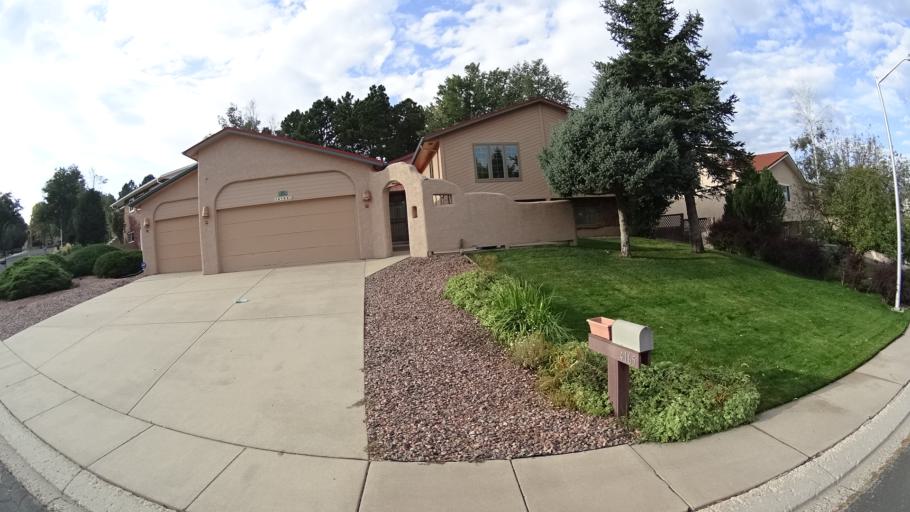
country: US
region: Colorado
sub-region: El Paso County
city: Cimarron Hills
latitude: 38.8701
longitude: -104.7501
